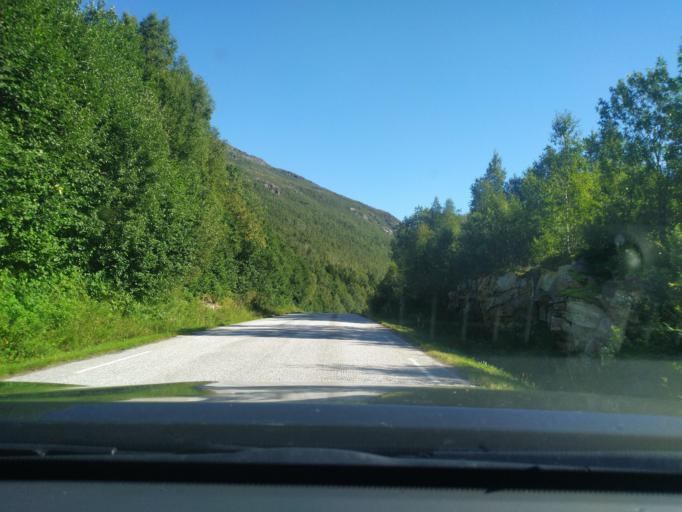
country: NO
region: Troms
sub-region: Dyroy
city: Brostadbotn
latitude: 68.9275
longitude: 17.6432
